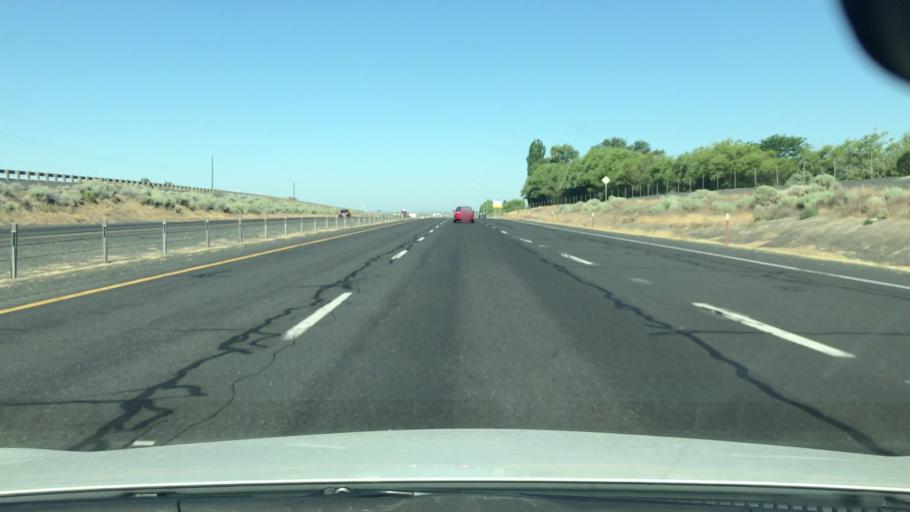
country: US
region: Washington
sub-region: Grant County
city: Cascade Valley
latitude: 47.1042
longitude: -119.3490
